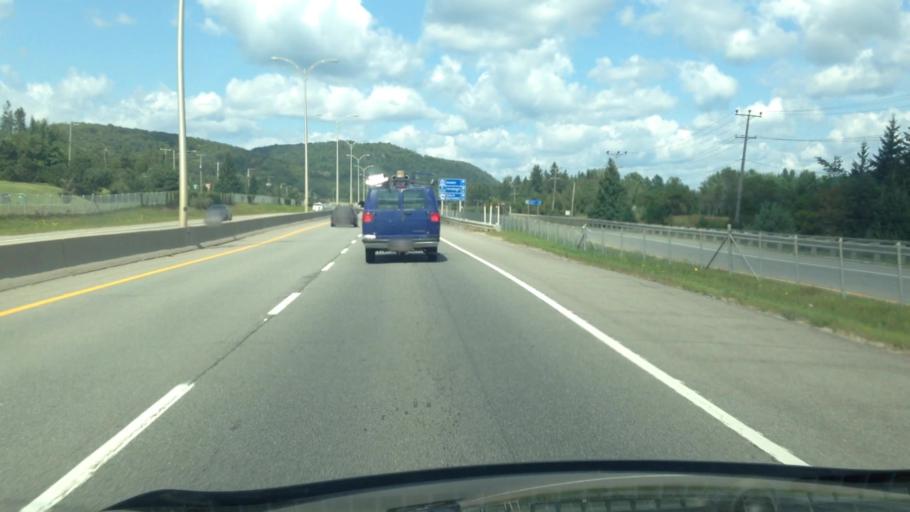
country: CA
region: Quebec
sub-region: Laurentides
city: Mont-Tremblant
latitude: 46.1242
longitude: -74.6081
